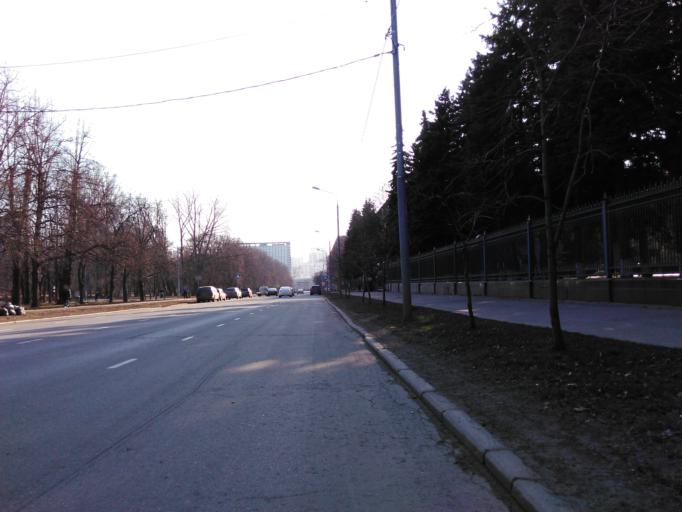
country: RU
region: Moscow
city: Vorob'yovo
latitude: 55.7103
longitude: 37.5182
